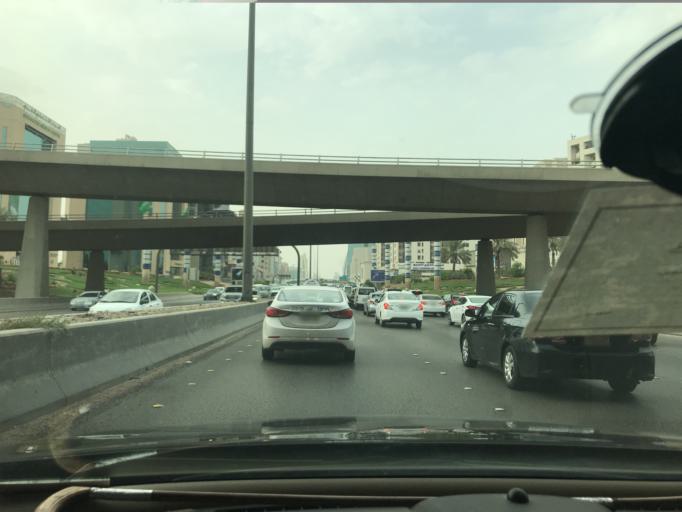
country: SA
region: Ar Riyad
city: Riyadh
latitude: 24.6788
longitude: 46.6889
